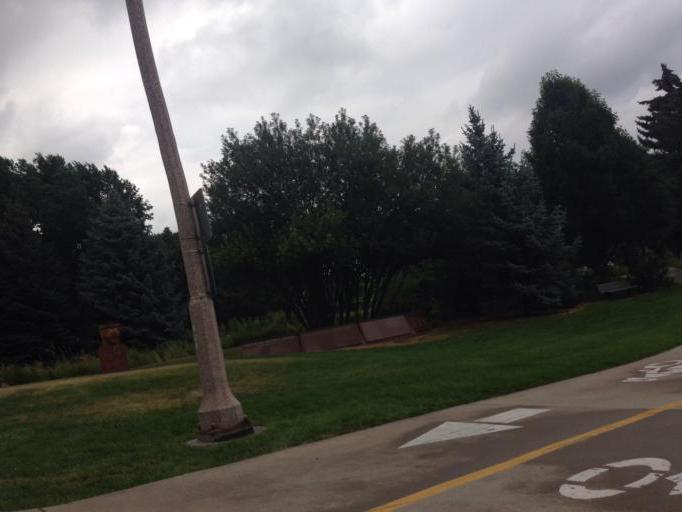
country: US
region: Colorado
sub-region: Larimer County
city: Fort Collins
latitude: 40.5753
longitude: -105.0866
